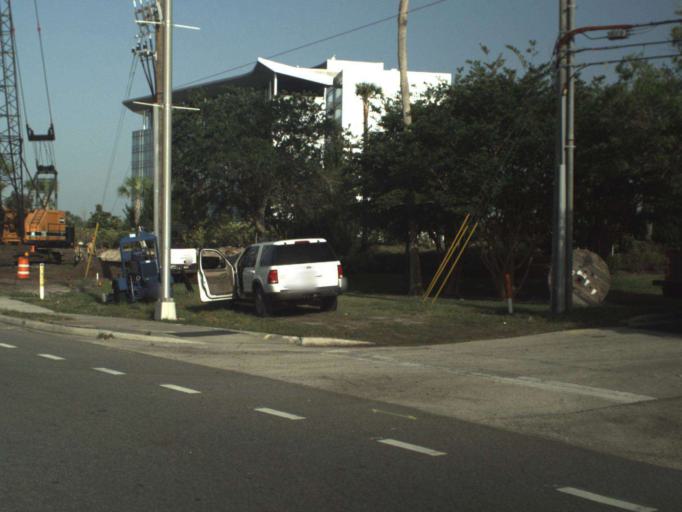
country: US
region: Florida
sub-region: Volusia County
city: Daytona Beach
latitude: 29.1925
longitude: -81.0686
